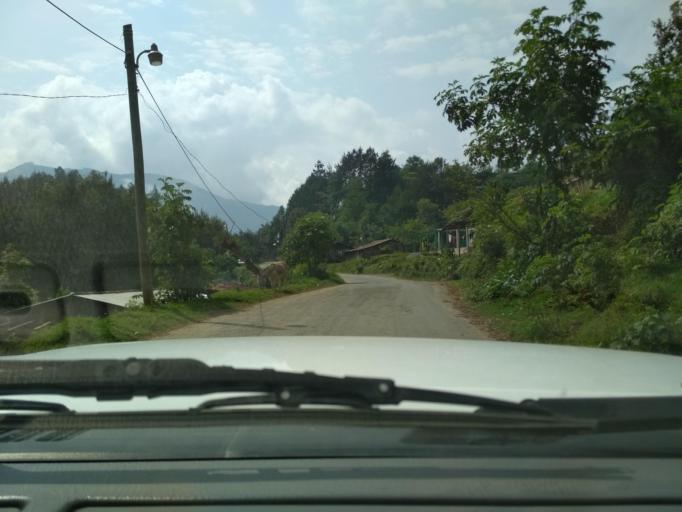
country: MX
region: Veracruz
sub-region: Camerino Z. Mendoza
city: Necoxtla
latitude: 18.7669
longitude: -97.1516
